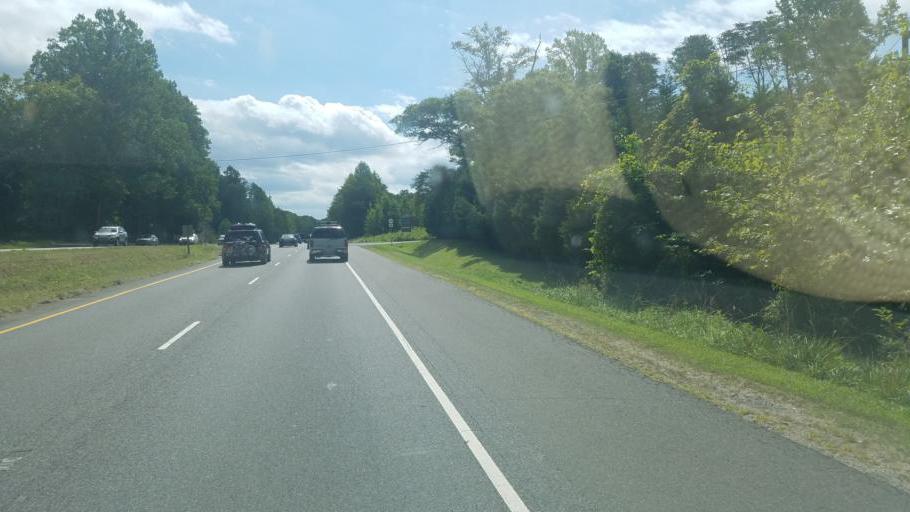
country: US
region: Virginia
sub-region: Stafford County
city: Falmouth
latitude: 38.4074
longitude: -77.5908
